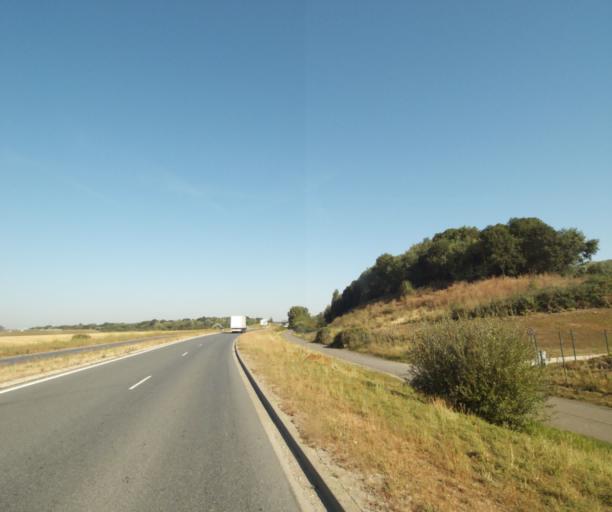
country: FR
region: Ile-de-France
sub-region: Departement de Seine-et-Marne
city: Combs-la-Ville
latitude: 48.6436
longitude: 2.5718
